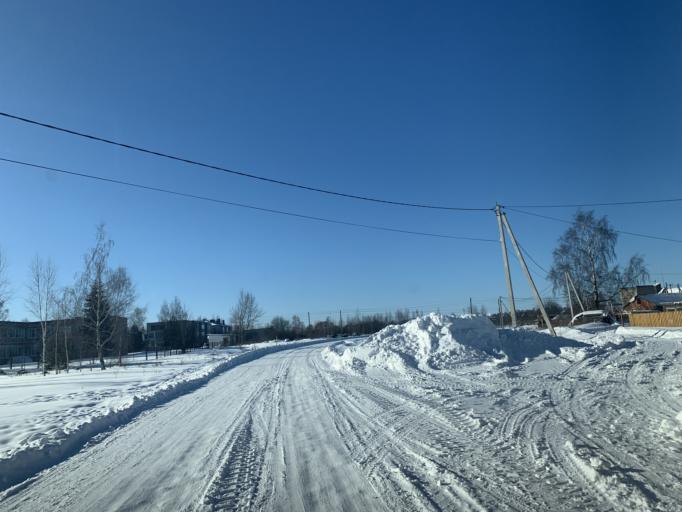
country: RU
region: Jaroslavl
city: Tunoshna
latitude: 57.6598
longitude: 40.0700
